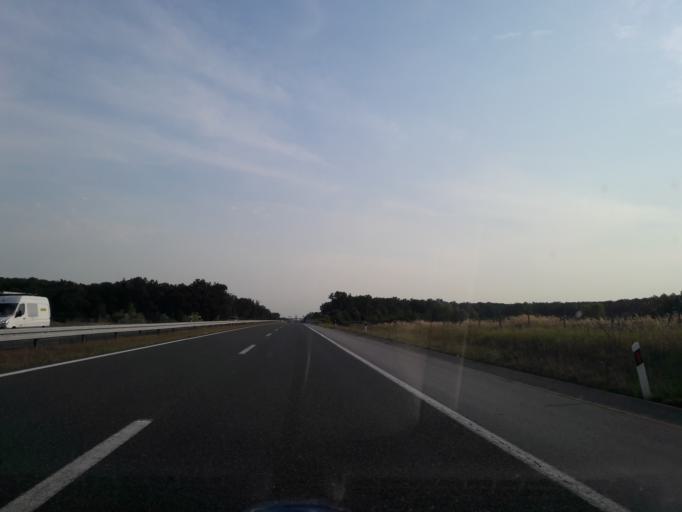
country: HR
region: Osjecko-Baranjska
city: Piskorevci
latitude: 45.2870
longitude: 18.3562
